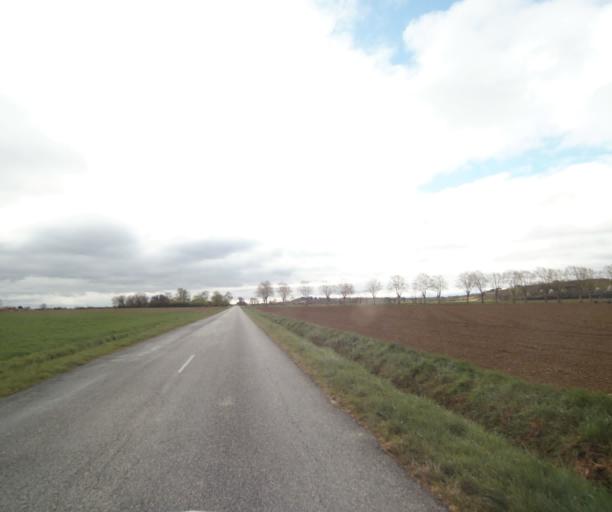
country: FR
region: Midi-Pyrenees
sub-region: Departement de l'Ariege
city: Saverdun
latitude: 43.2525
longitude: 1.5469
